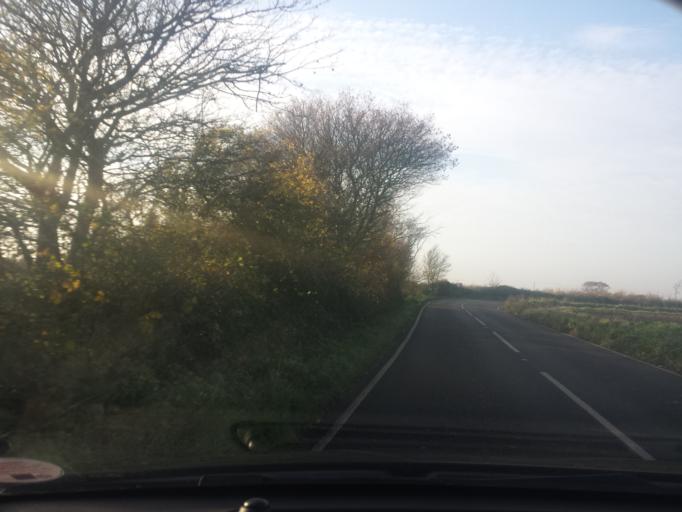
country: GB
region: England
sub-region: Essex
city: Saint Osyth
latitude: 51.7897
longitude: 1.0857
